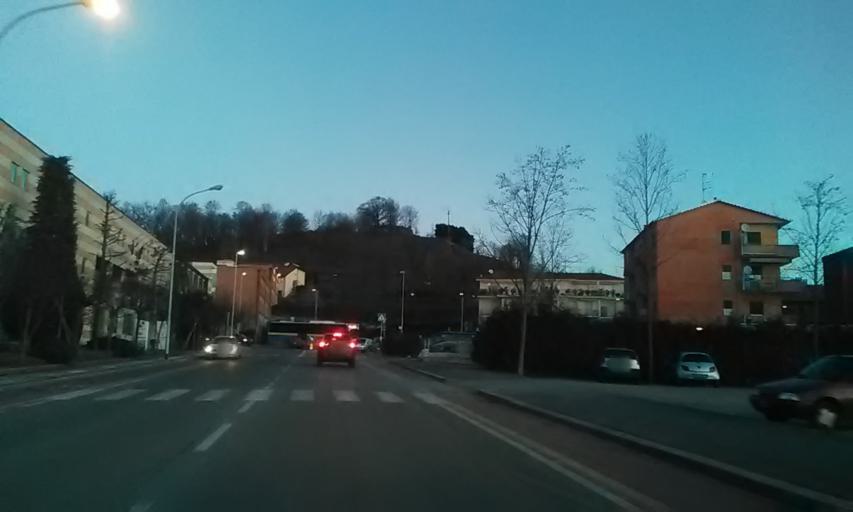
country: IT
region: Piedmont
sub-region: Provincia di Biella
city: Occhieppo Inferiore
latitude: 45.5562
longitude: 8.0345
